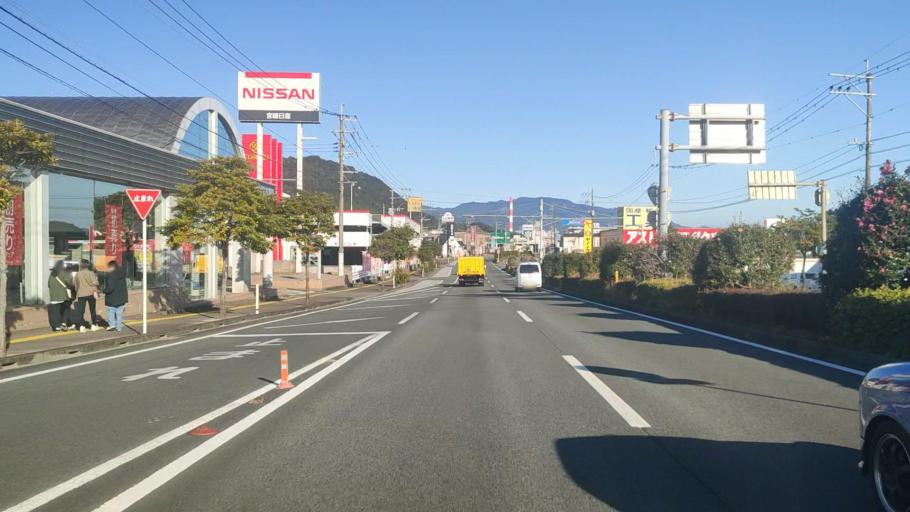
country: JP
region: Miyazaki
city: Nobeoka
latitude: 32.5460
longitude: 131.6776
